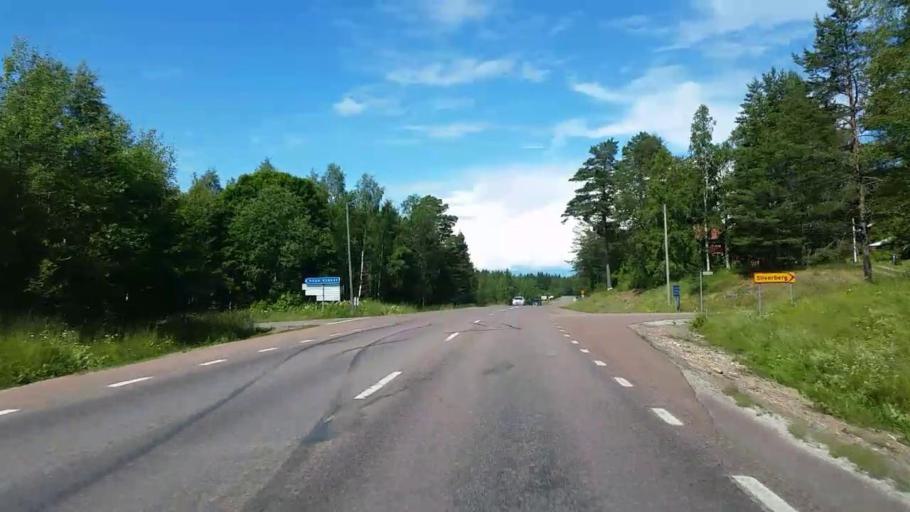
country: SE
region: Dalarna
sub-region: Rattviks Kommun
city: Raettvik
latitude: 61.0179
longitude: 15.2118
